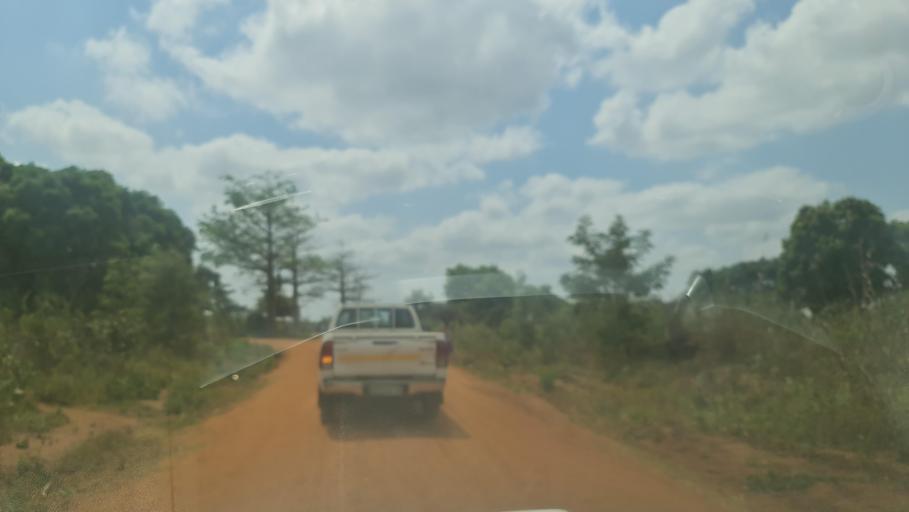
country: MW
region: Southern Region
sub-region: Nsanje District
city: Nsanje
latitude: -17.3953
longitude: 35.5720
